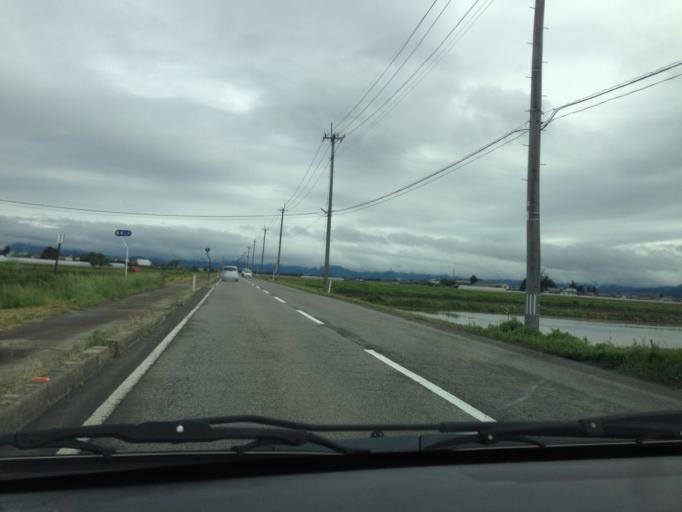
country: JP
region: Fukushima
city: Kitakata
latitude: 37.5460
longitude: 139.8561
